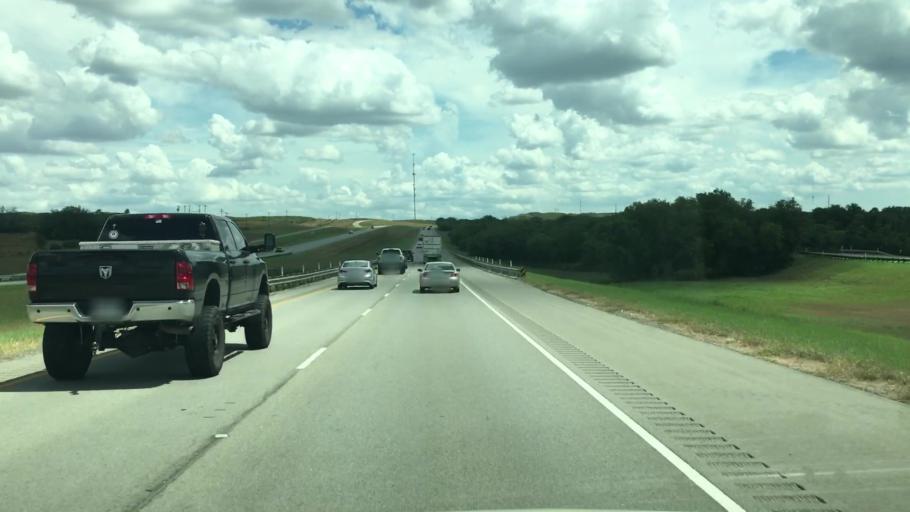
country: US
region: Texas
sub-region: San Patricio County
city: Mathis
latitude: 28.2624
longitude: -97.9317
